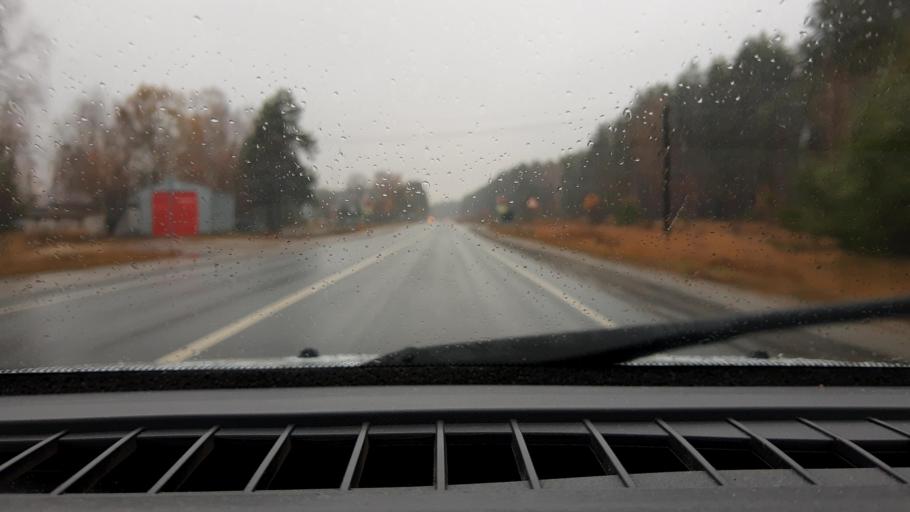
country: RU
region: Nizjnij Novgorod
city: Linda
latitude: 56.6903
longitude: 44.1872
